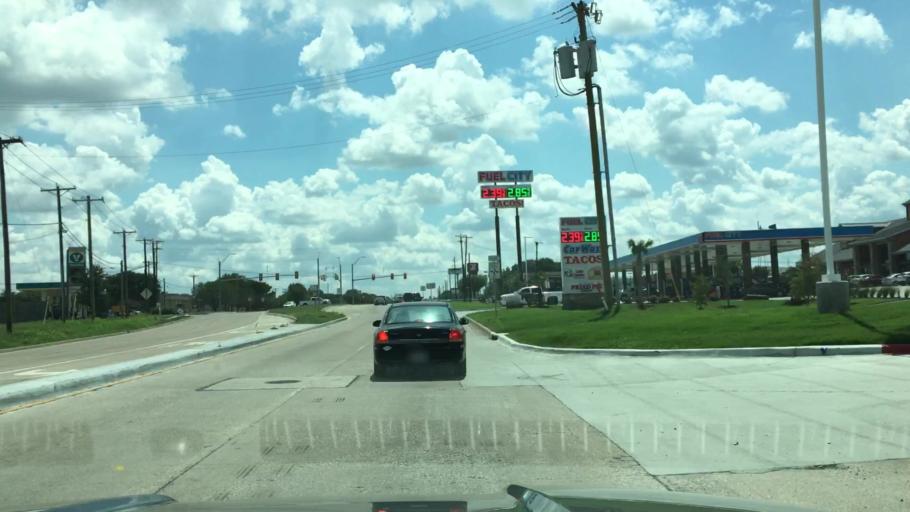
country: US
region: Texas
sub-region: Tarrant County
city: Blue Mound
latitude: 32.8495
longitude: -97.3432
